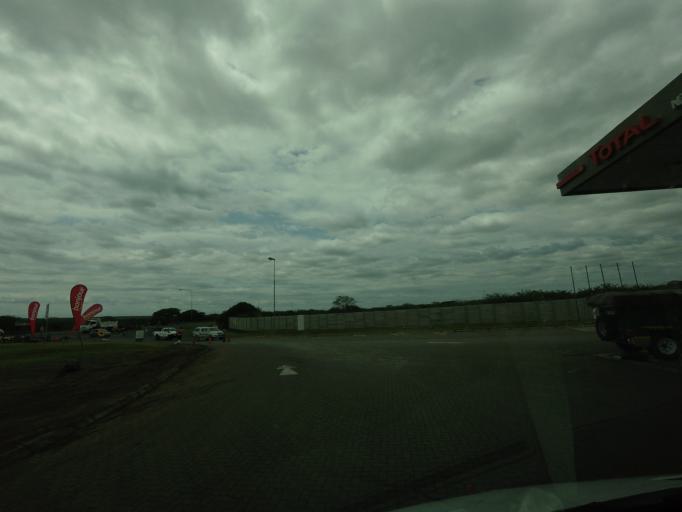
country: ZA
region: KwaZulu-Natal
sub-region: uMkhanyakude District Municipality
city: Hluhluwe
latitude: -28.0898
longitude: 32.2674
